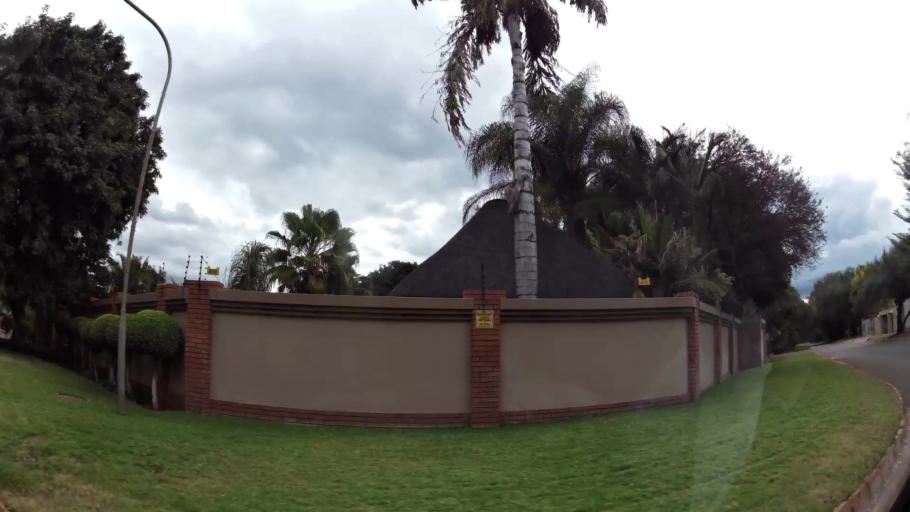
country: ZA
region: Limpopo
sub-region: Waterberg District Municipality
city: Mokopane
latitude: -24.2035
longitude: 29.0053
